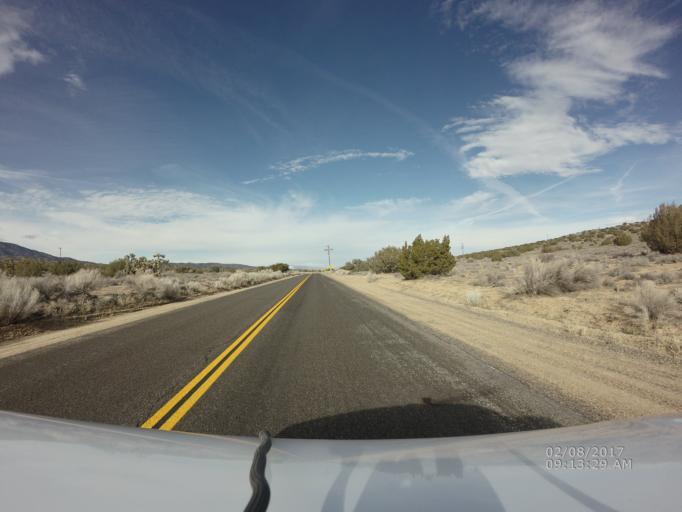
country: US
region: California
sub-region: Los Angeles County
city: Littlerock
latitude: 34.4640
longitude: -117.8822
